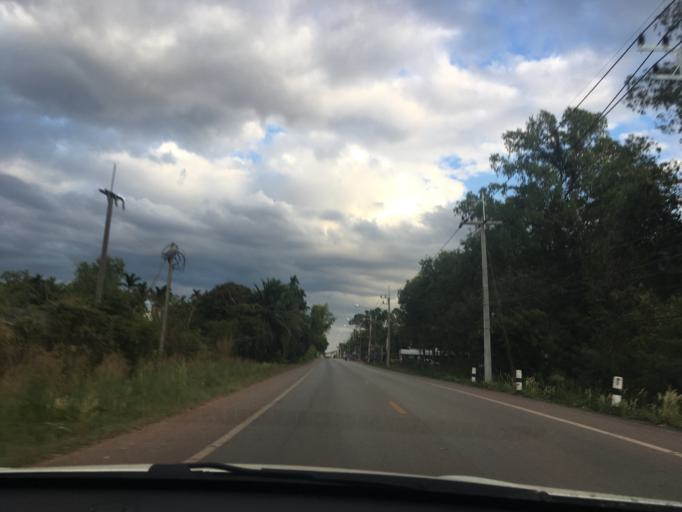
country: TH
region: Chanthaburi
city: Na Yai Am
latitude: 12.6922
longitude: 101.8090
